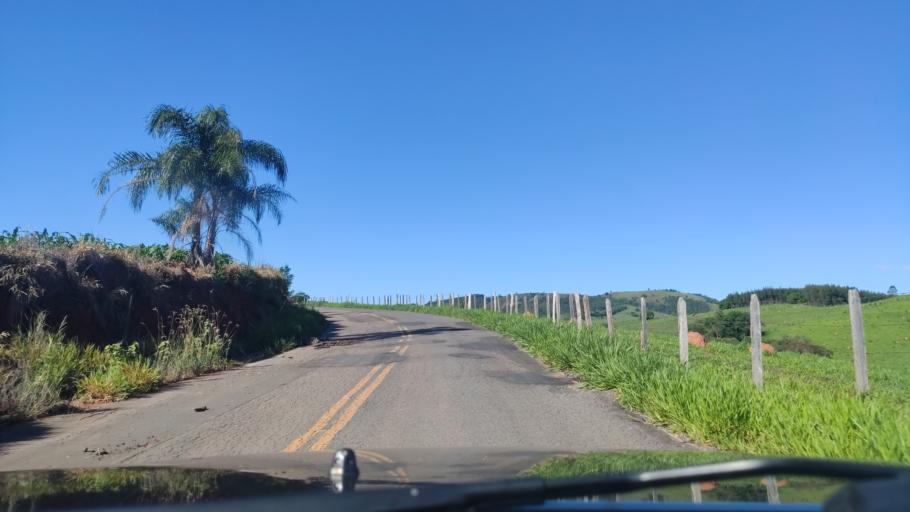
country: BR
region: Sao Paulo
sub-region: Aguas De Lindoia
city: Aguas de Lindoia
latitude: -22.5525
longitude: -46.6148
